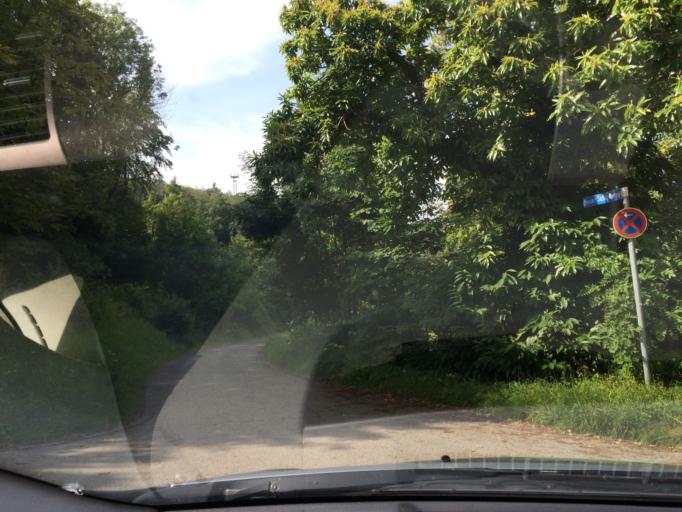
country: DE
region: North Rhine-Westphalia
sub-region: Regierungsbezirk Arnsberg
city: Nachrodt-Wiblingwerde
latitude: 51.3445
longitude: 7.5699
